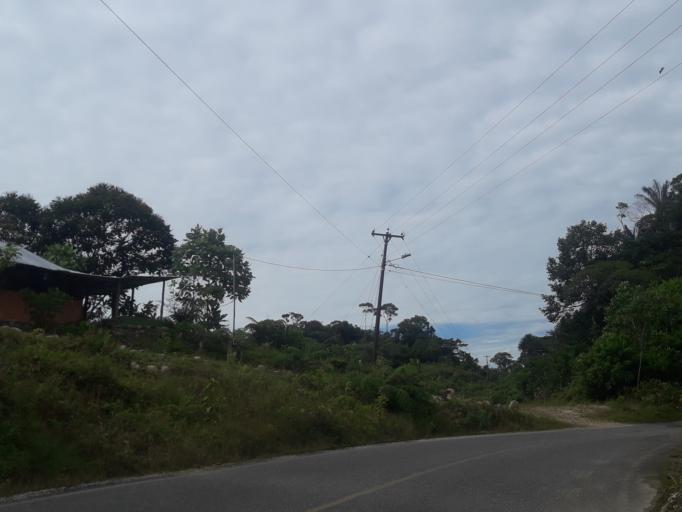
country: EC
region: Napo
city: Tena
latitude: -1.0526
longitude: -77.8954
